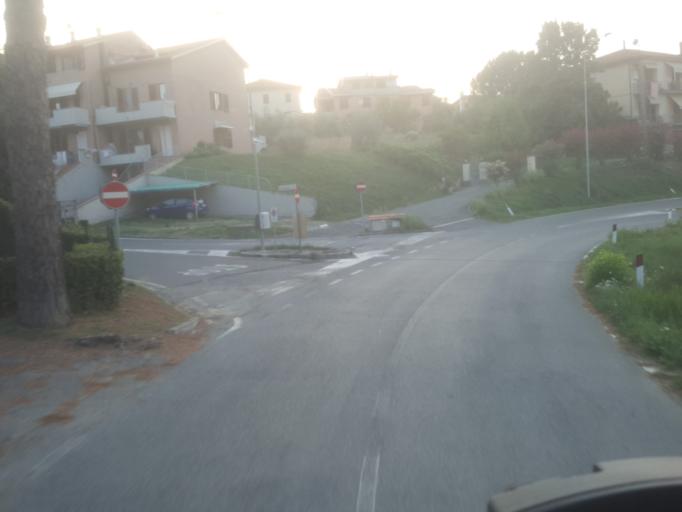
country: IT
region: Tuscany
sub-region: Province of Florence
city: Certaldo
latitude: 43.5388
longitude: 11.0338
